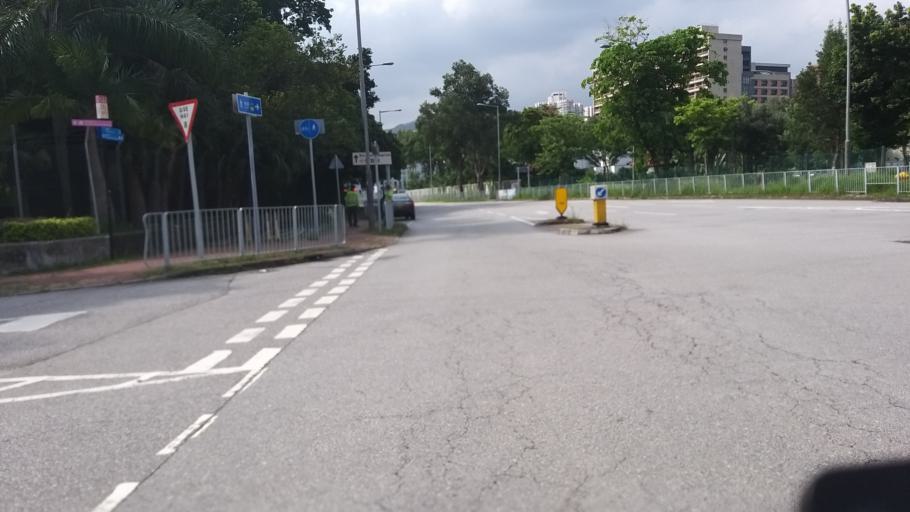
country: HK
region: Tuen Mun
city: Tuen Mun
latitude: 22.4065
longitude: 113.9748
